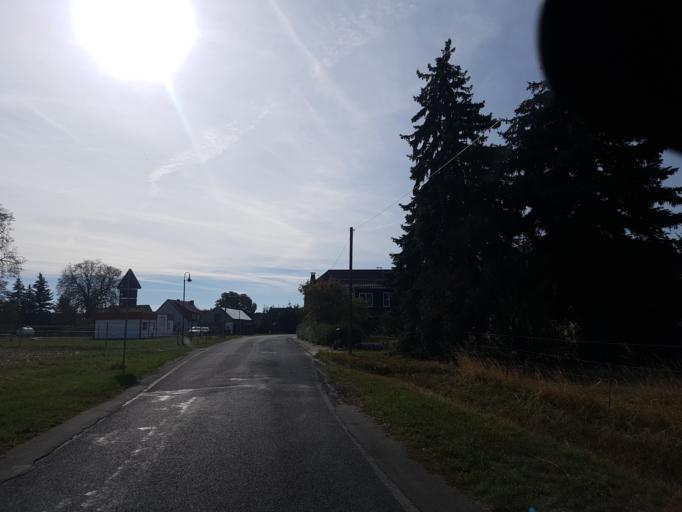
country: DE
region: Brandenburg
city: Schlieben
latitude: 51.7795
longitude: 13.3223
